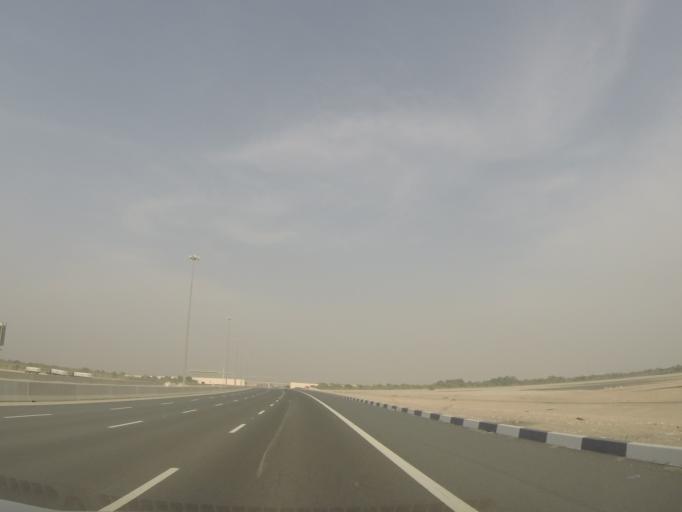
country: AE
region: Abu Dhabi
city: Abu Dhabi
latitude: 24.6986
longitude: 54.7658
